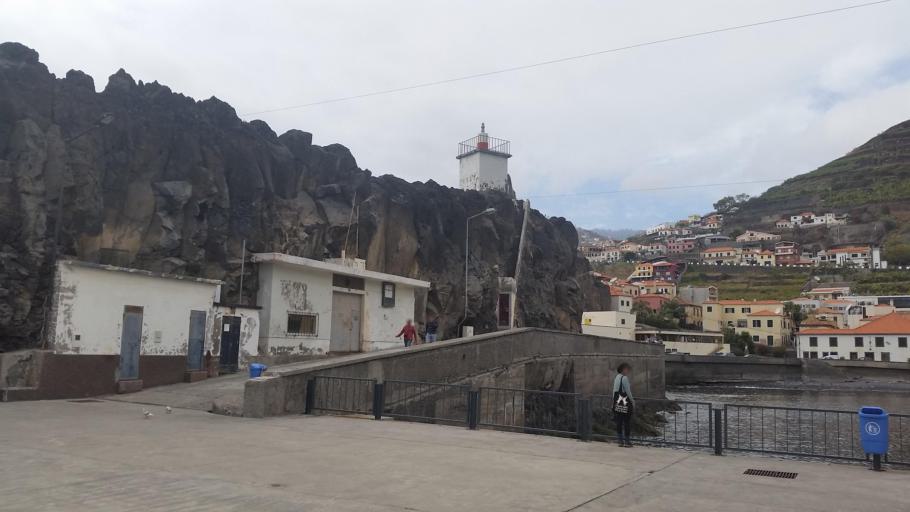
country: PT
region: Madeira
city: Camara de Lobos
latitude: 32.6466
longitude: -16.9753
